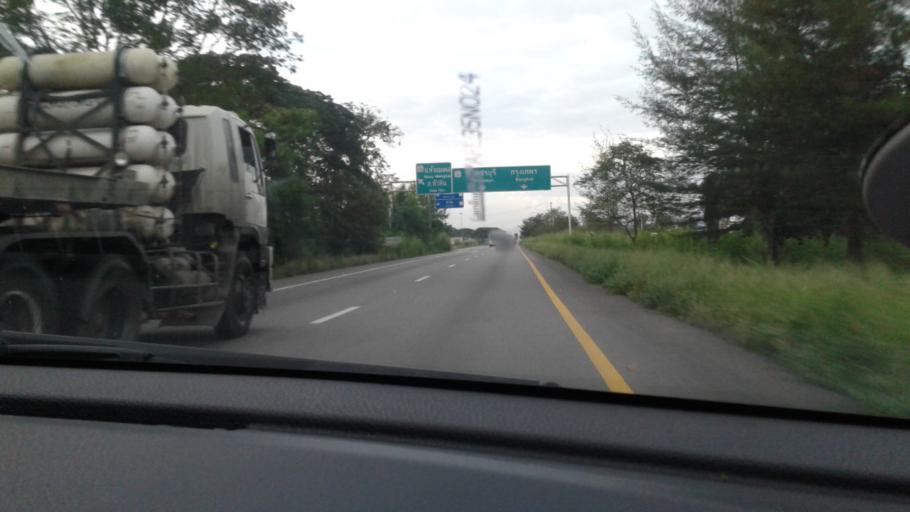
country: TH
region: Prachuap Khiri Khan
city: Hua Hin
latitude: 12.5699
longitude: 99.8679
